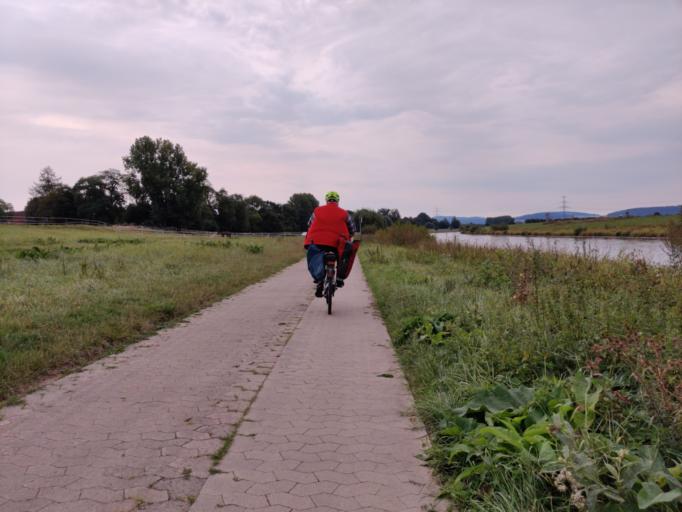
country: DE
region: Lower Saxony
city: Hehlen
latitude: 52.0343
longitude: 9.4247
